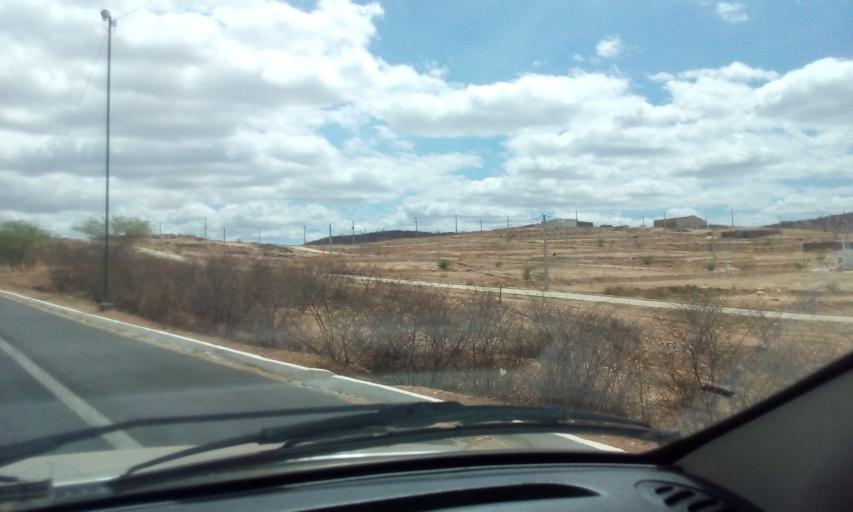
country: BR
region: Rio Grande do Norte
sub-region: Currais Novos
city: Currais Novos
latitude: -6.2580
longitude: -36.5001
